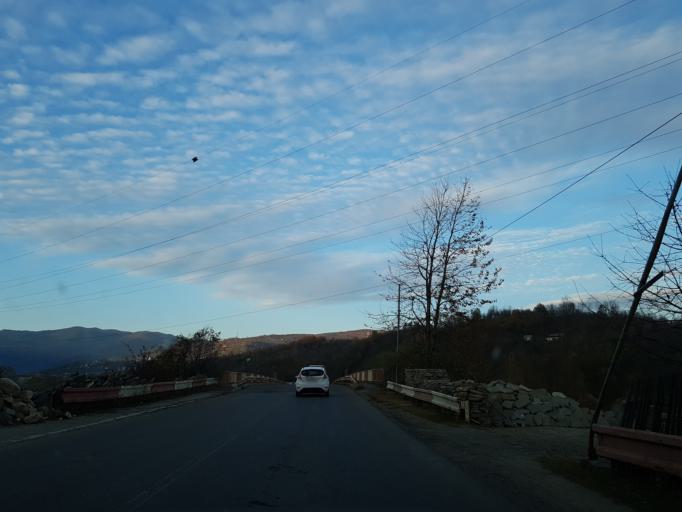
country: RO
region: Prahova
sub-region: Oras Breaza
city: Gura Beliei
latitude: 45.2230
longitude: 25.6388
